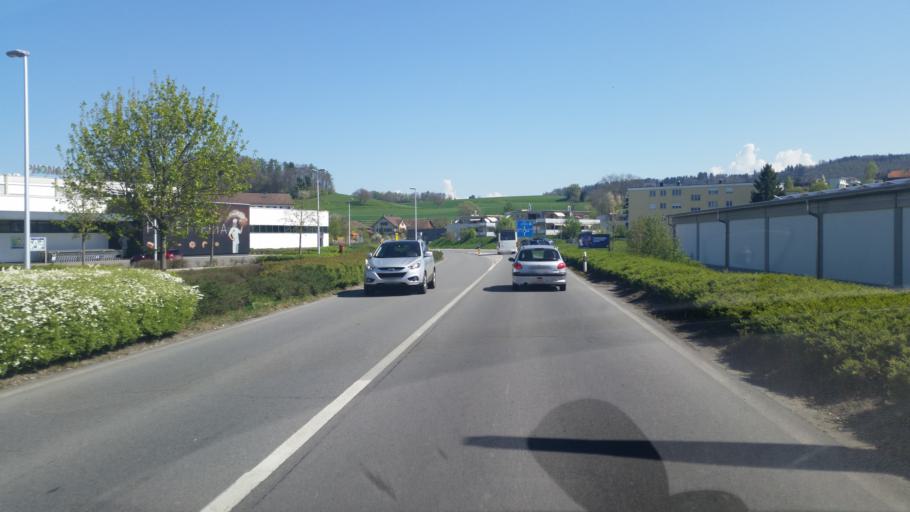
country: CH
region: Fribourg
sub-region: See District
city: Murten
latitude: 46.9313
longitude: 7.1268
